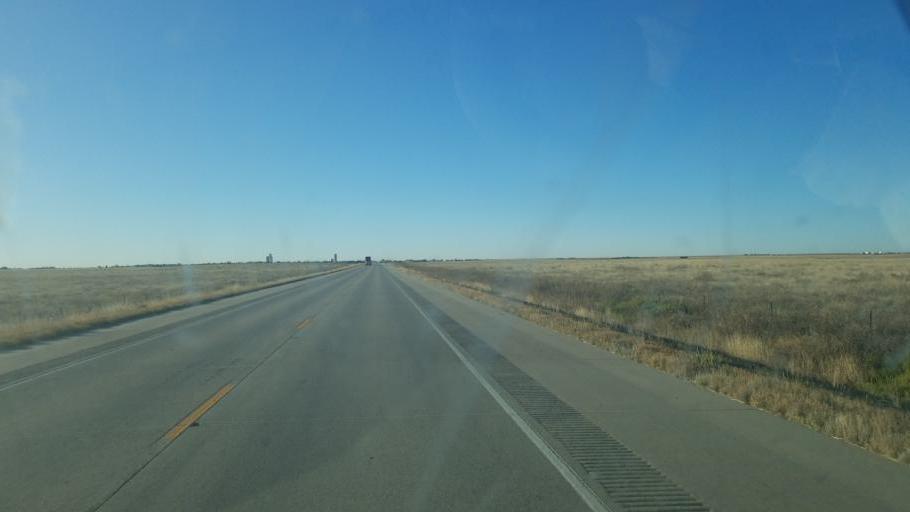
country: US
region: Colorado
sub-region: Kiowa County
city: Eads
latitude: 38.5091
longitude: -102.7857
